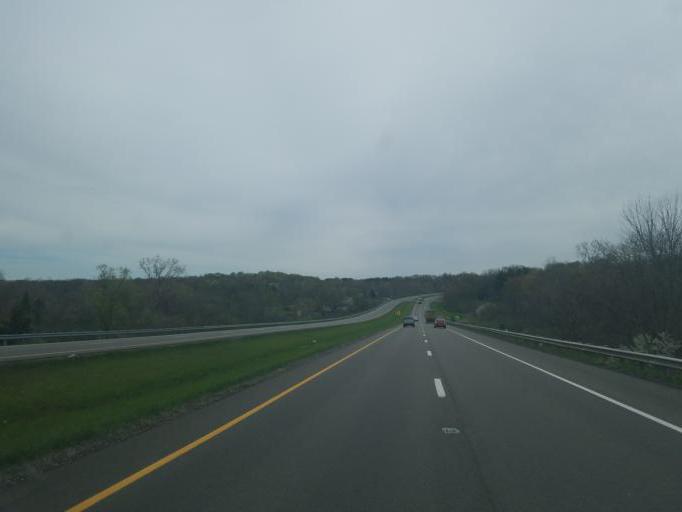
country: US
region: Ohio
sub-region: Wayne County
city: Doylestown
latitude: 40.9855
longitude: -81.6828
